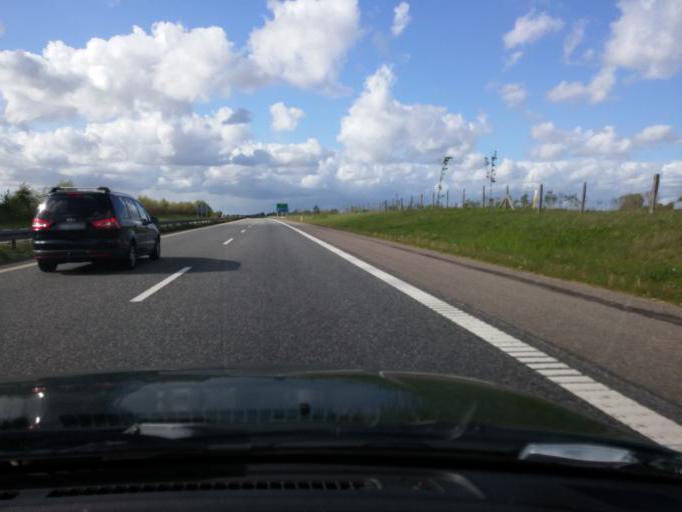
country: DK
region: South Denmark
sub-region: Faaborg-Midtfyn Kommune
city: Ringe
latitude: 55.2630
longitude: 10.4691
